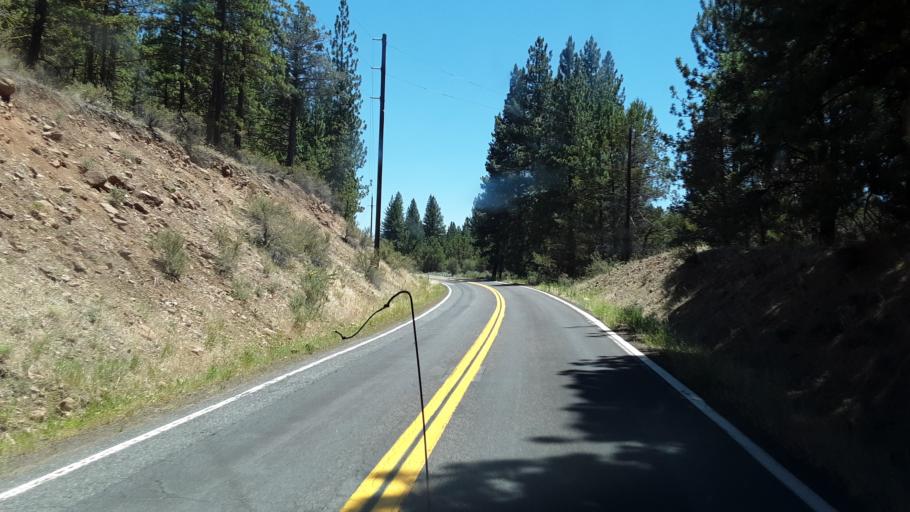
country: US
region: California
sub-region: Modoc County
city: Alturas
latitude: 41.0823
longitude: -120.8992
